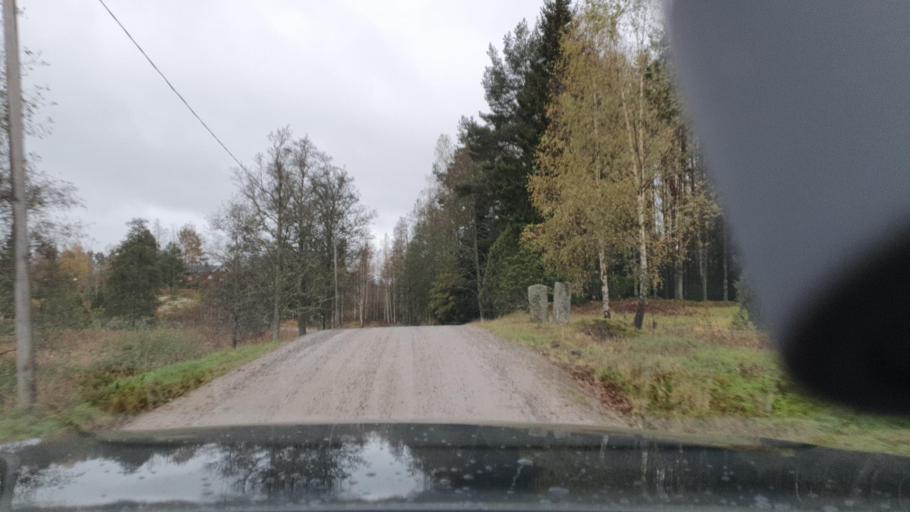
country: SE
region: Vaermland
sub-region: Karlstads Kommun
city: Edsvalla
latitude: 59.6059
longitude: 12.9173
